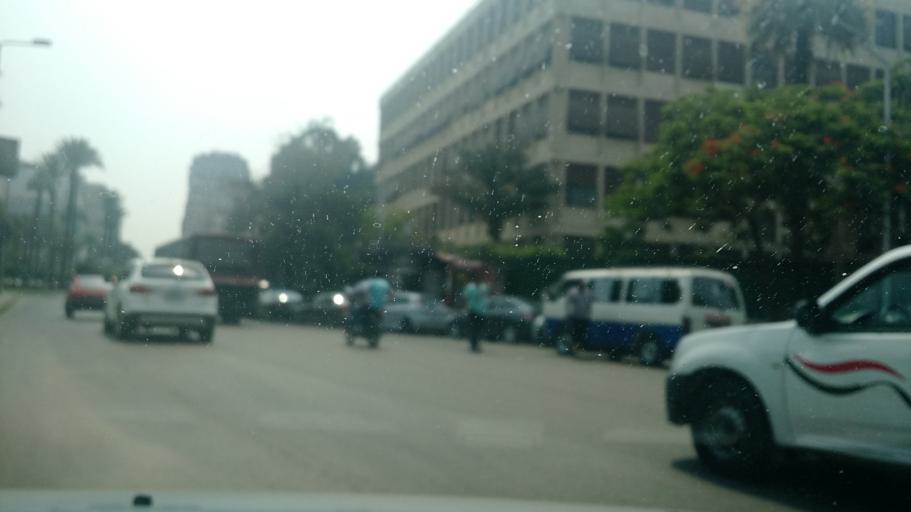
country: EG
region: Al Jizah
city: Al Jizah
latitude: 30.0275
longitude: 31.2112
